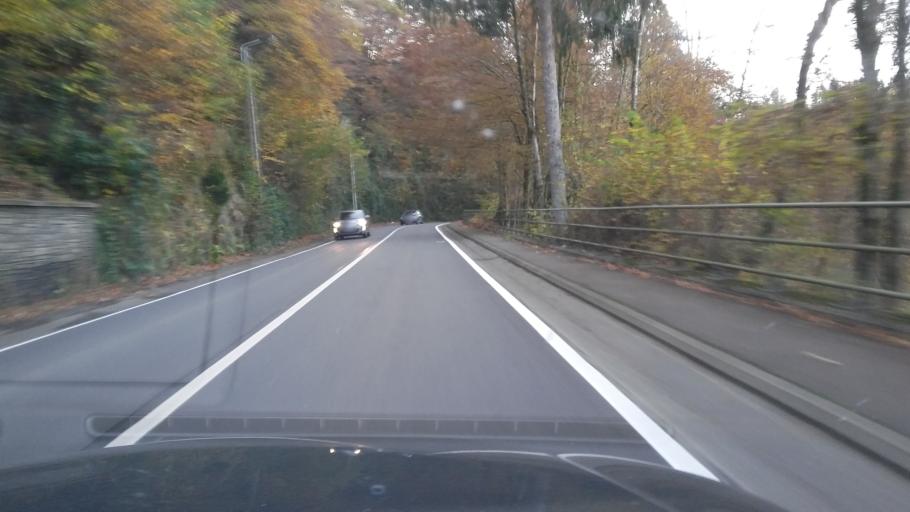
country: BE
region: Wallonia
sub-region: Province du Luxembourg
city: Bouillon
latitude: 49.7844
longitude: 5.0674
